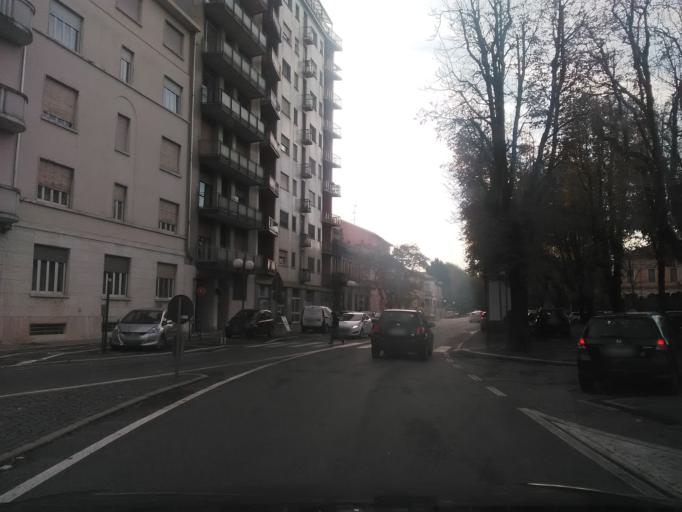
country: IT
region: Piedmont
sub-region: Provincia di Vercelli
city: Vercelli
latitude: 45.3212
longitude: 8.4257
